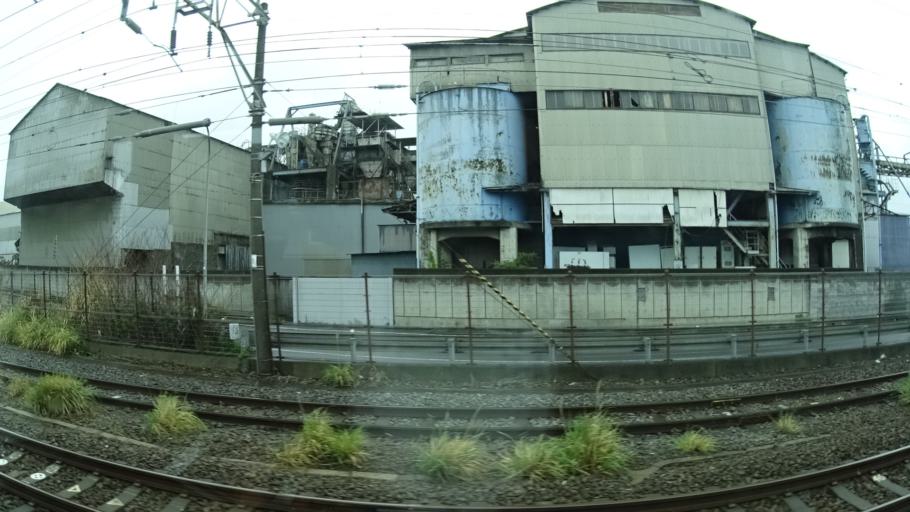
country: JP
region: Ibaraki
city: Hitachi
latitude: 36.5938
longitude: 140.6635
